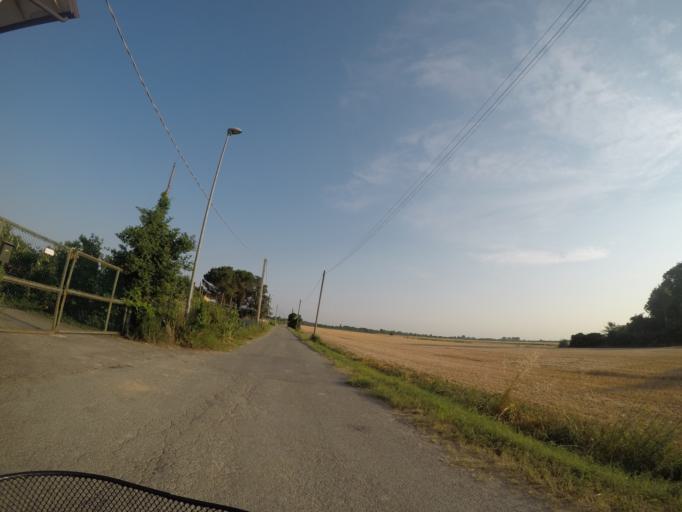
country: IT
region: Veneto
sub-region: Provincia di Rovigo
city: Fratta Polesine
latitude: 45.0201
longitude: 11.6620
